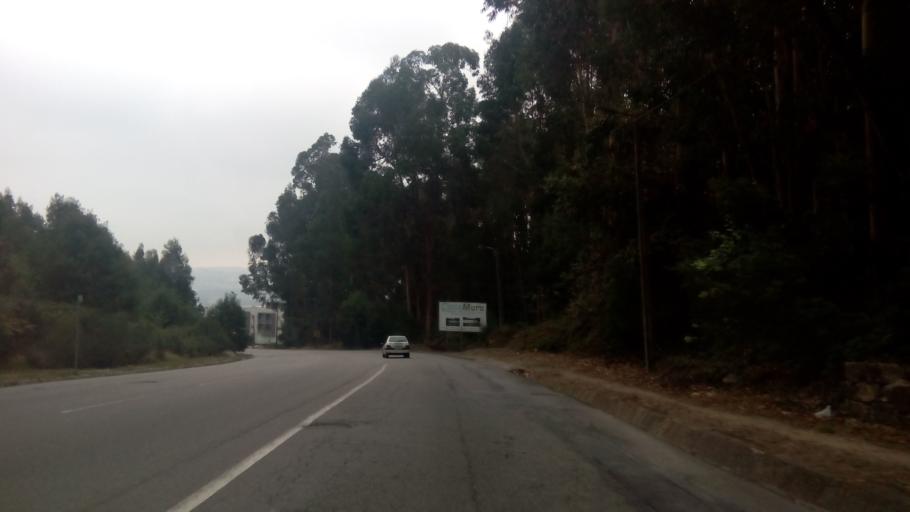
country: PT
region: Porto
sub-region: Paredes
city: Madalena
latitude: 41.2163
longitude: -8.3578
